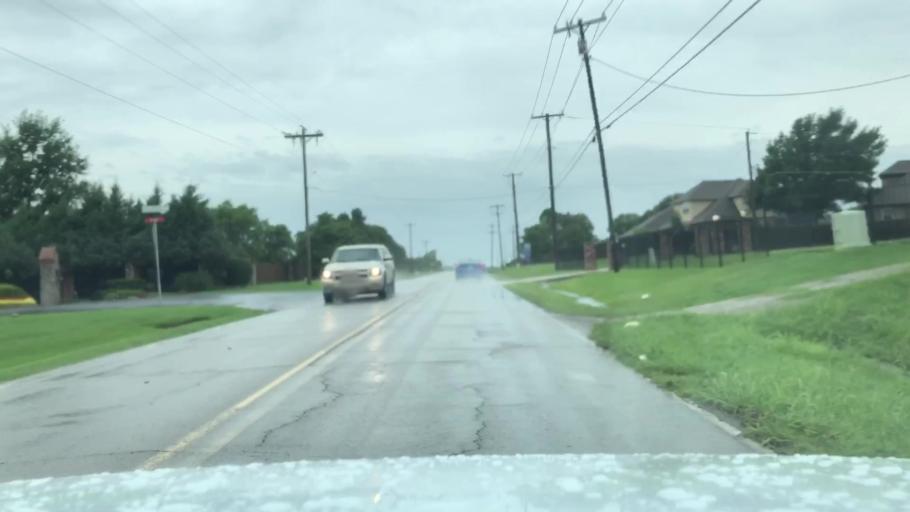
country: US
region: Oklahoma
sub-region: Tulsa County
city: Jenks
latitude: 36.0028
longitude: -96.0005
